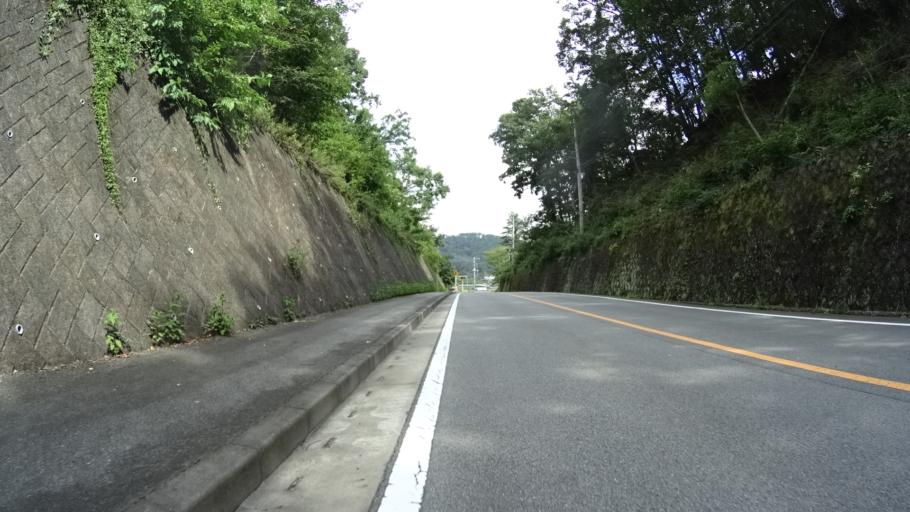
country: JP
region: Yamanashi
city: Kofu-shi
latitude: 35.7067
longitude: 138.5551
